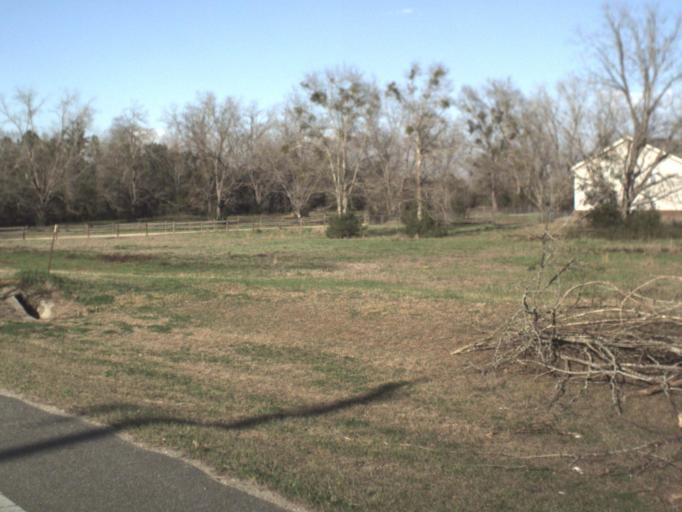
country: US
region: Florida
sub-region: Jackson County
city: Marianna
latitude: 30.7573
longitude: -85.2295
